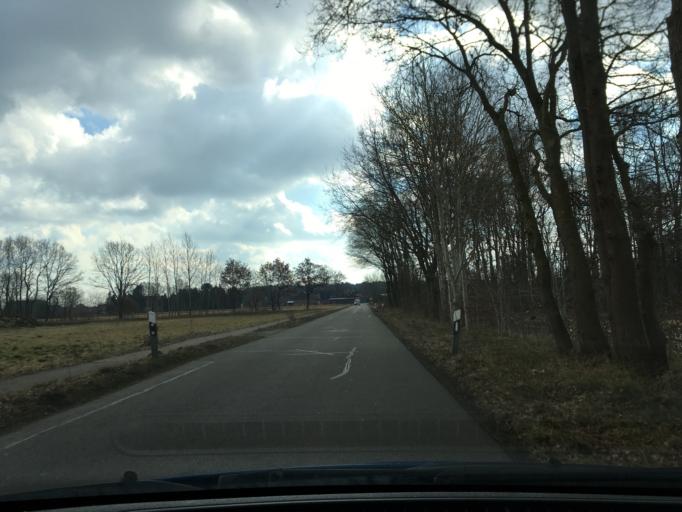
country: DE
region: Lower Saxony
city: Handorf
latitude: 53.3306
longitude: 10.3534
